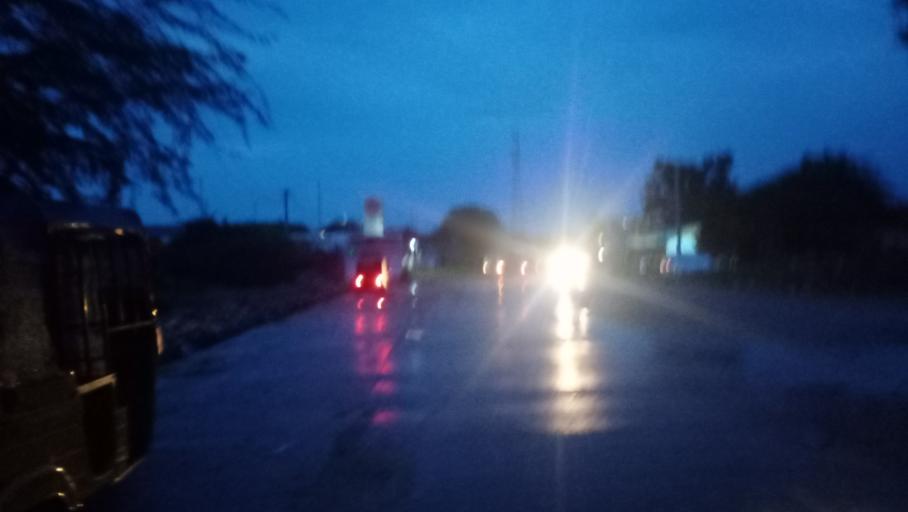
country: IN
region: Karnataka
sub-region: Tumkur
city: Pavagada
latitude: 13.9404
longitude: 77.2764
